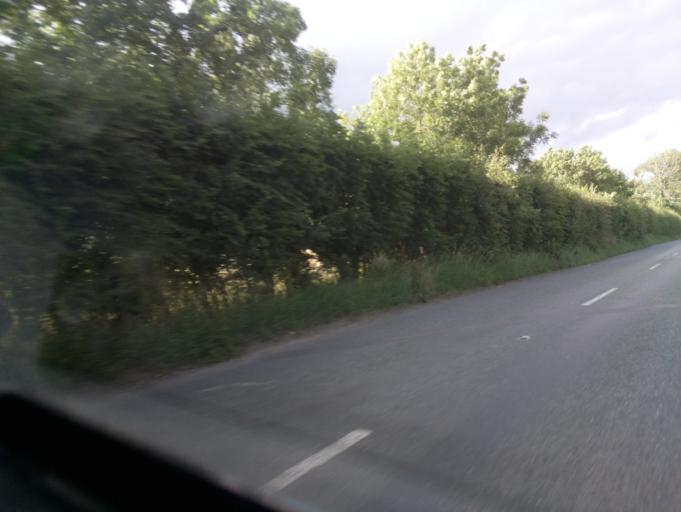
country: GB
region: England
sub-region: Gloucestershire
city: Chipping Campden
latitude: 52.0243
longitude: -1.7428
